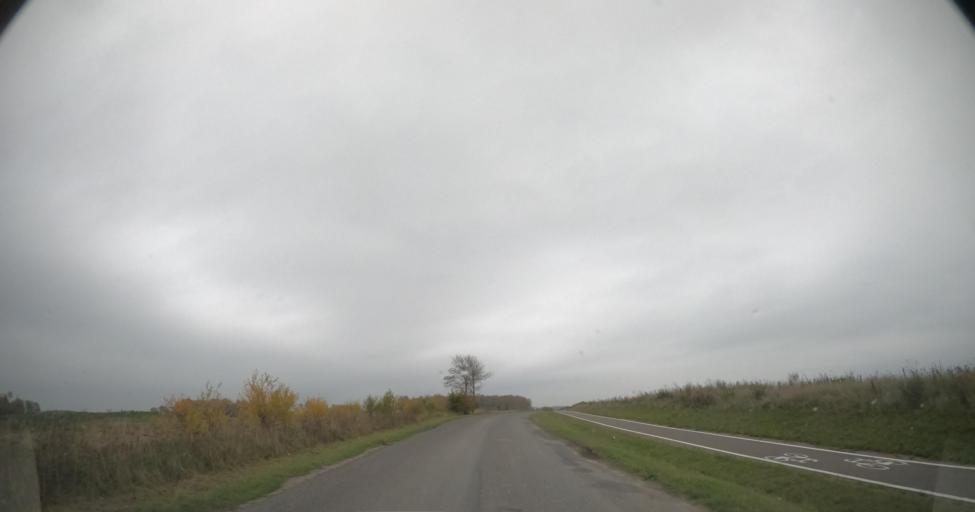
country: PL
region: West Pomeranian Voivodeship
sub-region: Powiat lobeski
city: Wegorzyno
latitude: 53.4963
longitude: 15.6303
